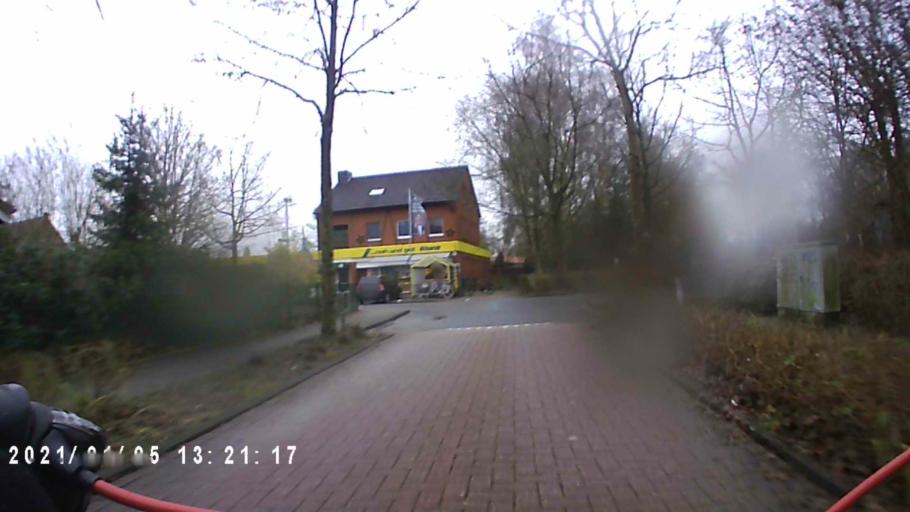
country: DE
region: Lower Saxony
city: Leer
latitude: 53.2327
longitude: 7.4386
